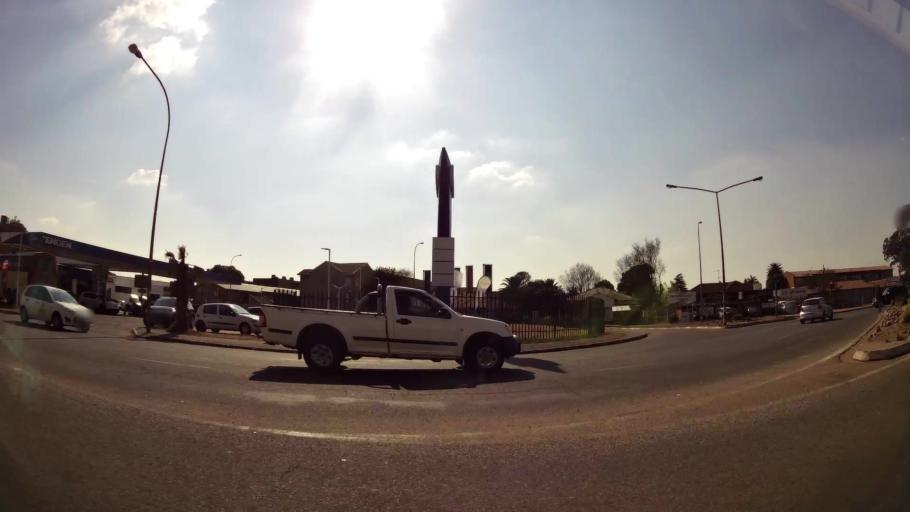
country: ZA
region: Gauteng
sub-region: City of Johannesburg Metropolitan Municipality
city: Modderfontein
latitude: -26.1072
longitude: 28.2361
